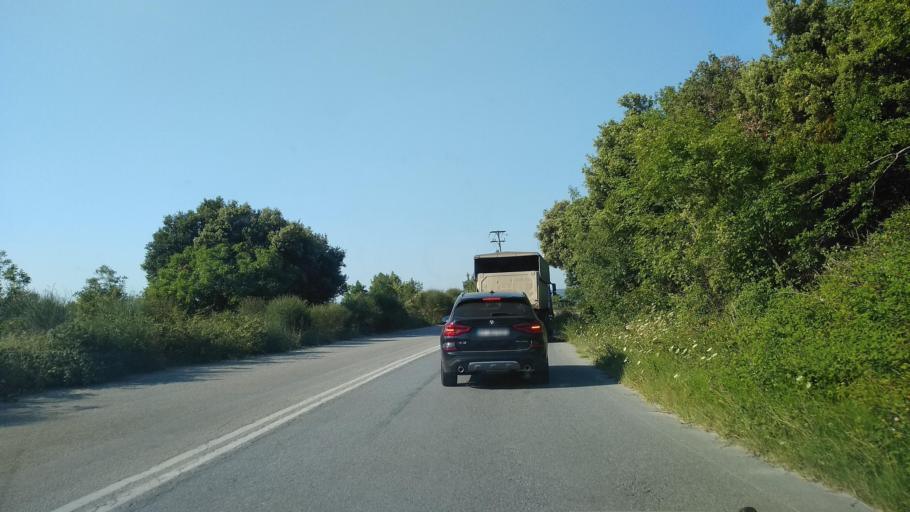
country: GR
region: Central Macedonia
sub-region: Nomos Chalkidikis
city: Stratonion
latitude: 40.5227
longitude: 23.8243
